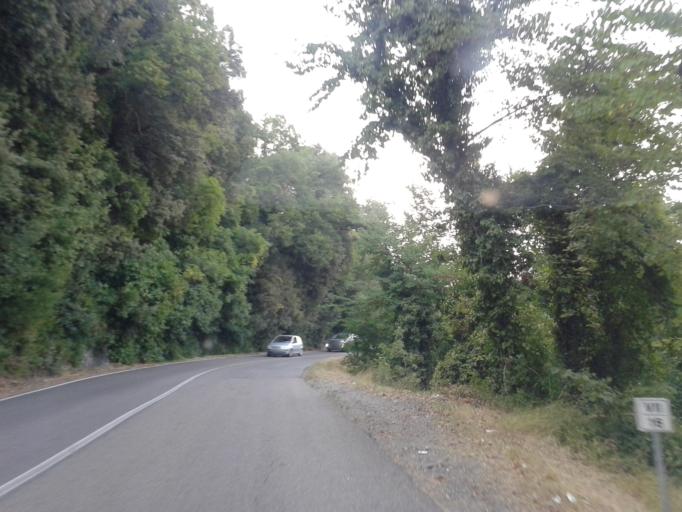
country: IT
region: Tuscany
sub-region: Provincia di Livorno
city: Rosignano Marittimo
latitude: 43.4027
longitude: 10.4885
